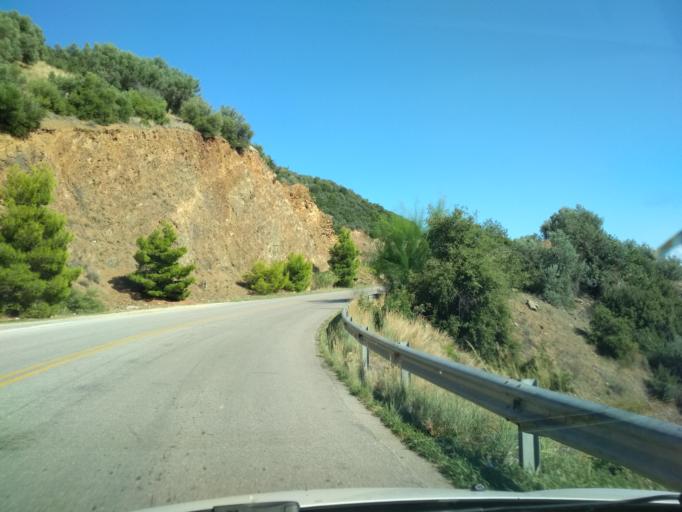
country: GR
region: Central Greece
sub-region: Nomos Evvoias
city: Oreoi
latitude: 38.8494
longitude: 23.0649
